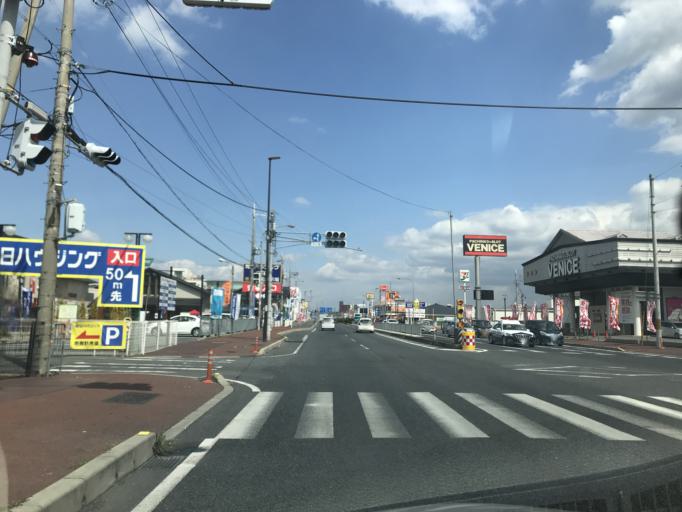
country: JP
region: Nara
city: Nara-shi
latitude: 34.6747
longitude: 135.8004
